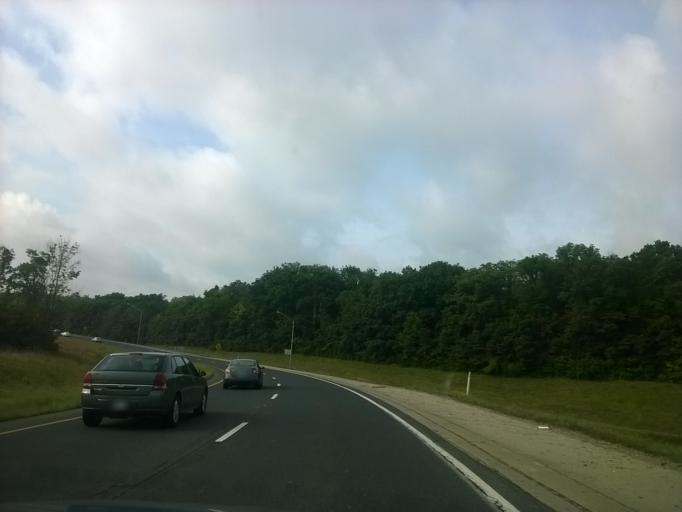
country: US
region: Indiana
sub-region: Boone County
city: Zionsville
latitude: 39.9296
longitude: -86.2686
